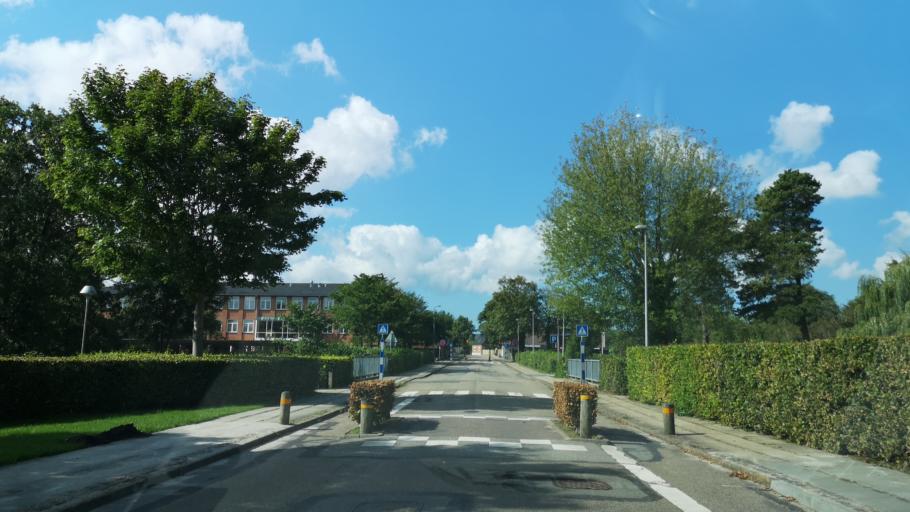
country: DK
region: Central Jutland
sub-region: Ringkobing-Skjern Kommune
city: Skjern
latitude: 55.9466
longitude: 8.5013
